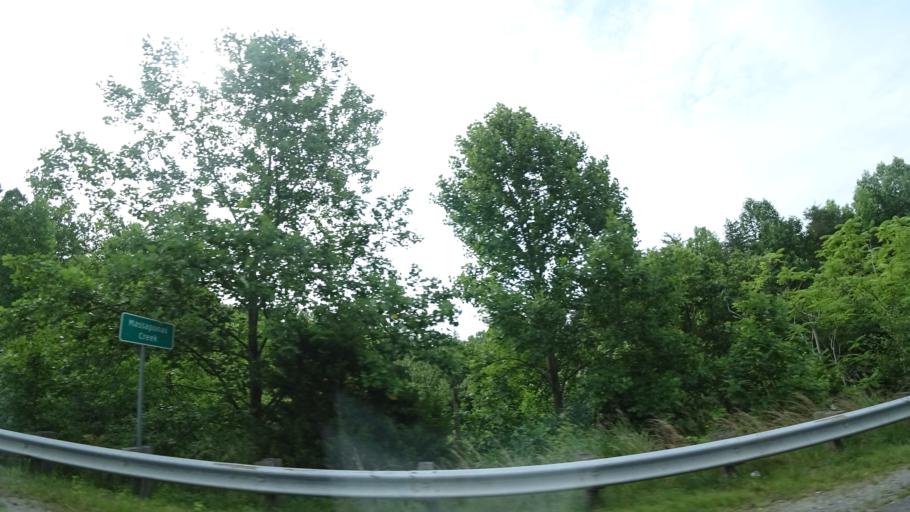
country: US
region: Virginia
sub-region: Spotsylvania County
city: Spotsylvania
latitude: 38.2417
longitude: -77.5353
